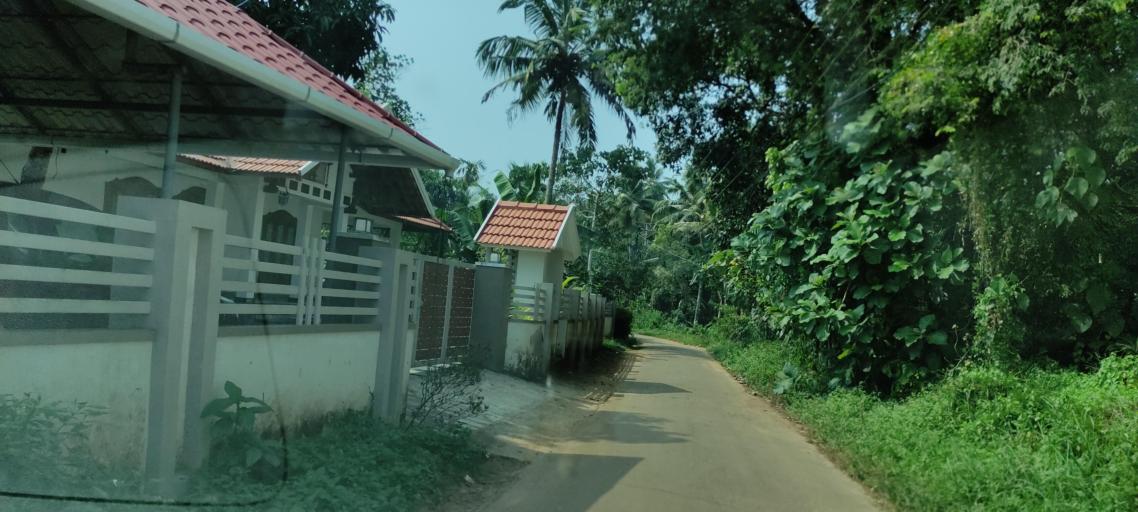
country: IN
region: Kerala
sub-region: Pattanamtitta
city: Adur
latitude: 9.2124
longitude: 76.6891
